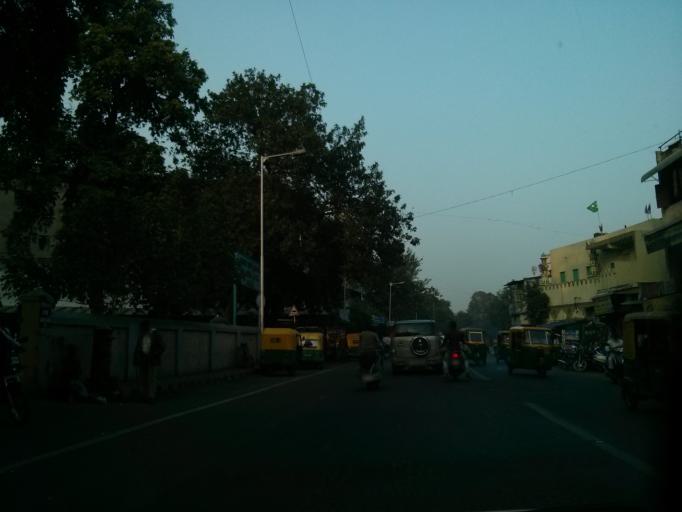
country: IN
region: Gujarat
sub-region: Ahmadabad
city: Ahmedabad
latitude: 23.0328
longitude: 72.5846
